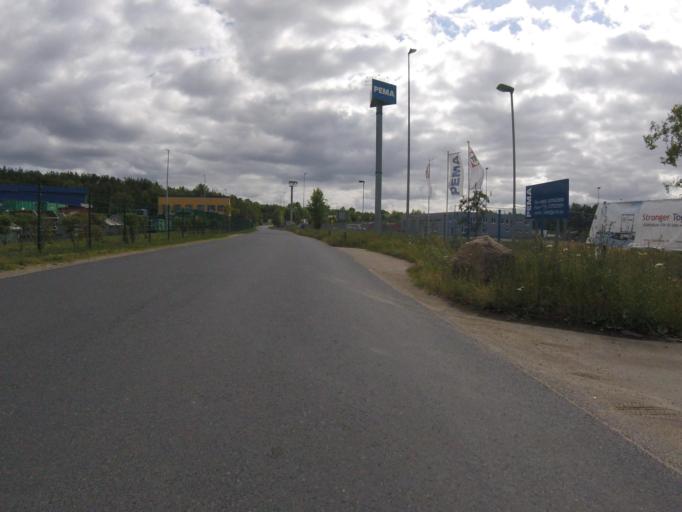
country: DE
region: Brandenburg
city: Wildau
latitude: 52.3177
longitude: 13.6712
